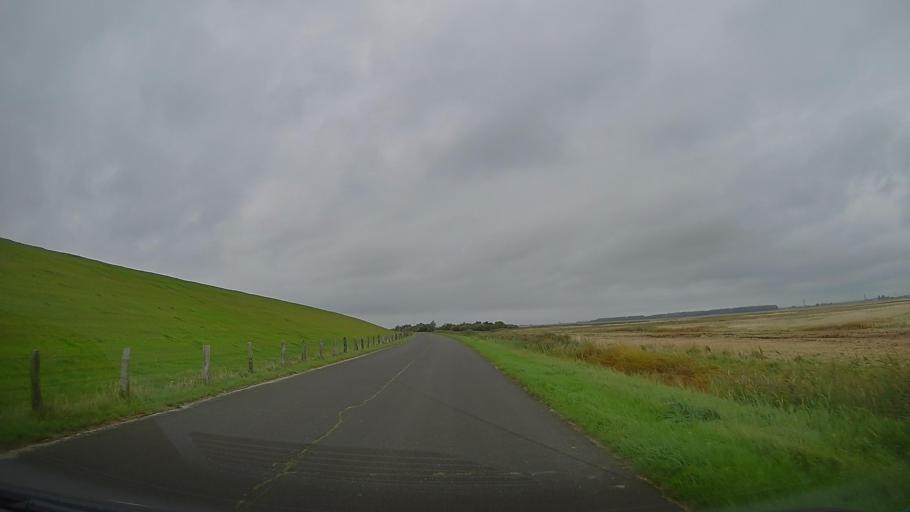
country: DE
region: Schleswig-Holstein
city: Busenwurth
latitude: 54.0445
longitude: 8.9819
